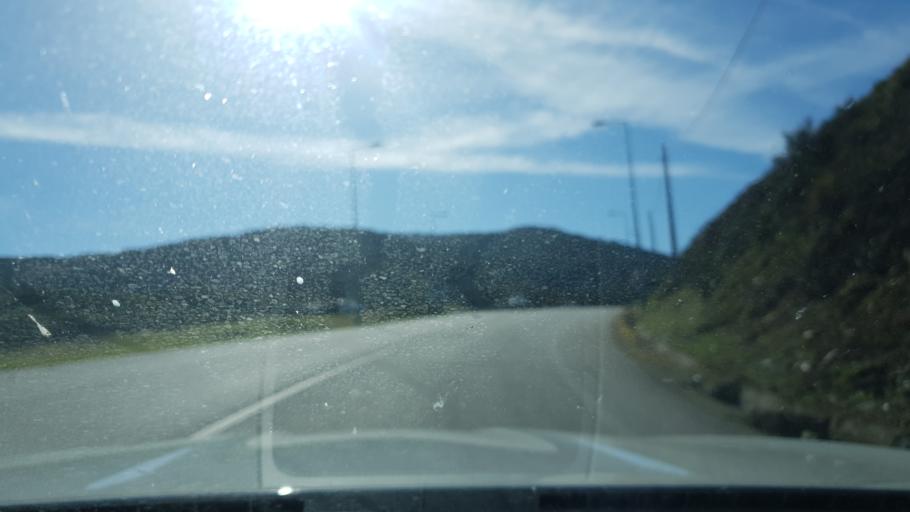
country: PT
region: Braganca
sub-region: Torre de Moncorvo
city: Torre de Moncorvo
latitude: 41.1823
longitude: -7.1014
